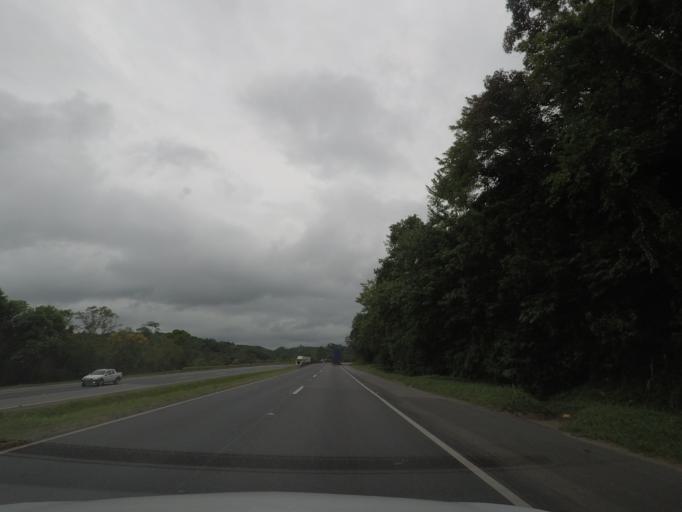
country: BR
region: Sao Paulo
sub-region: Juquia
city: Juquia
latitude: -24.3657
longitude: -47.6930
